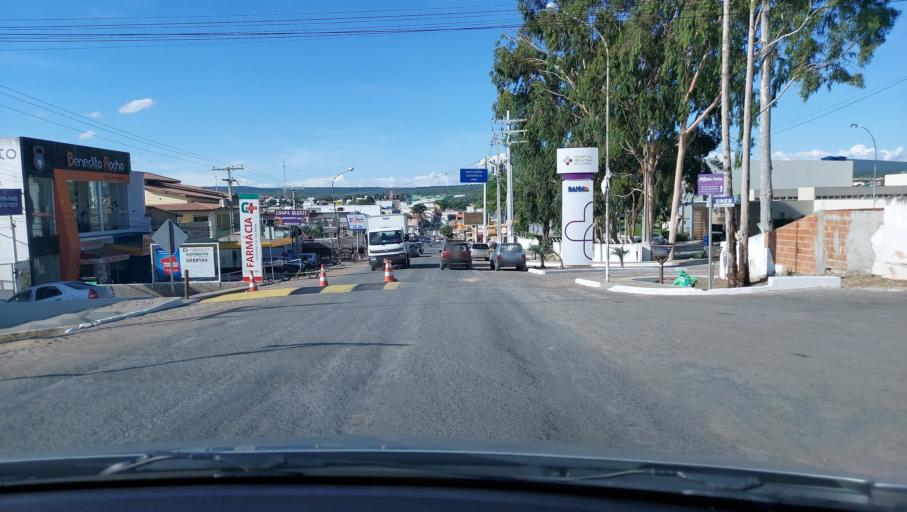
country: BR
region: Bahia
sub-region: Seabra
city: Seabra
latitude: -12.4258
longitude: -41.7693
